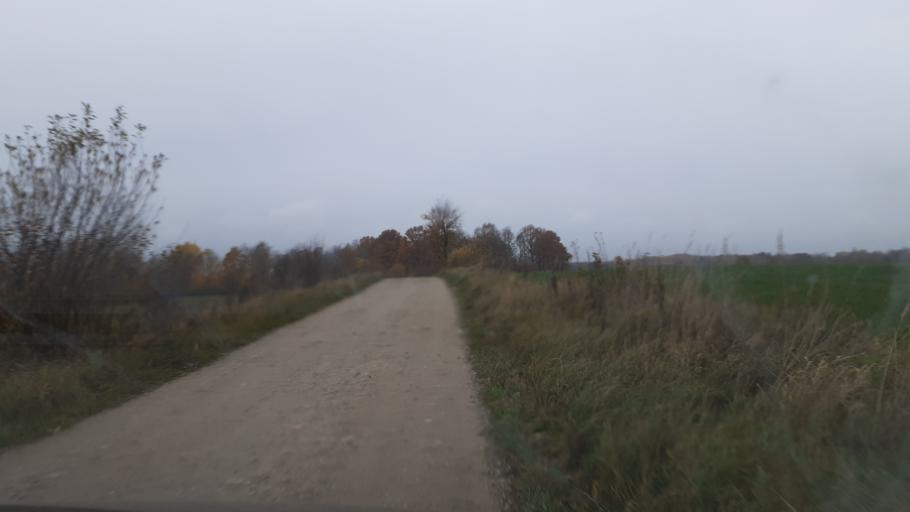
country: LV
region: Saldus Rajons
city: Saldus
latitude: 56.8681
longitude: 22.3416
